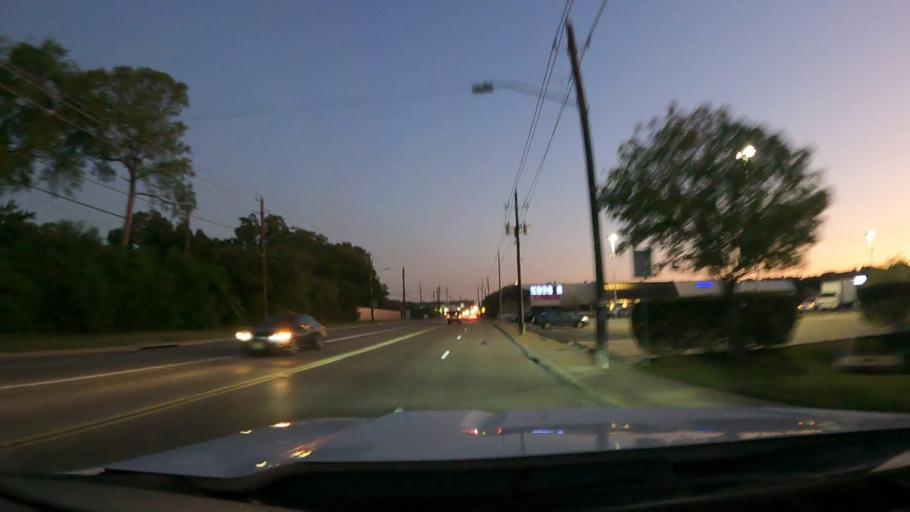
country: US
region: Texas
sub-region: Tarrant County
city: Pantego
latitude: 32.7321
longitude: -97.1492
